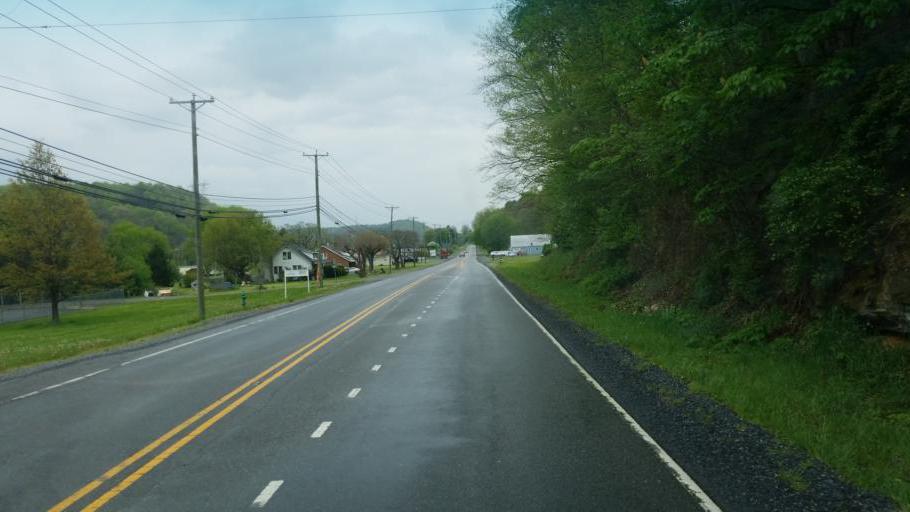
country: US
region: Virginia
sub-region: Smyth County
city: Atkins
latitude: 36.8572
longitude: -81.4645
